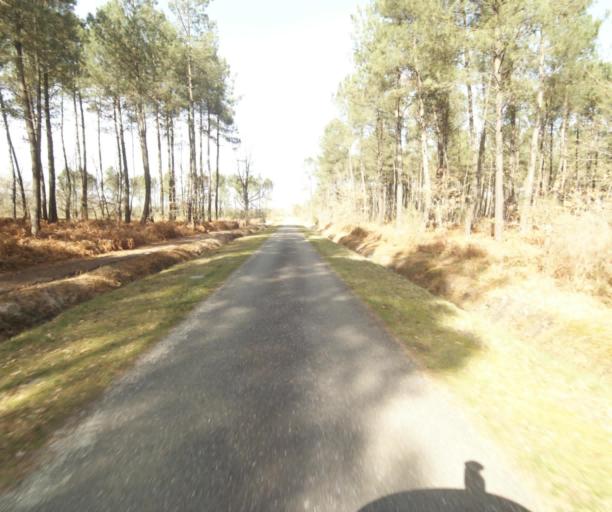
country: FR
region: Aquitaine
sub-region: Departement des Landes
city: Roquefort
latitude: 44.1422
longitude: -0.2041
